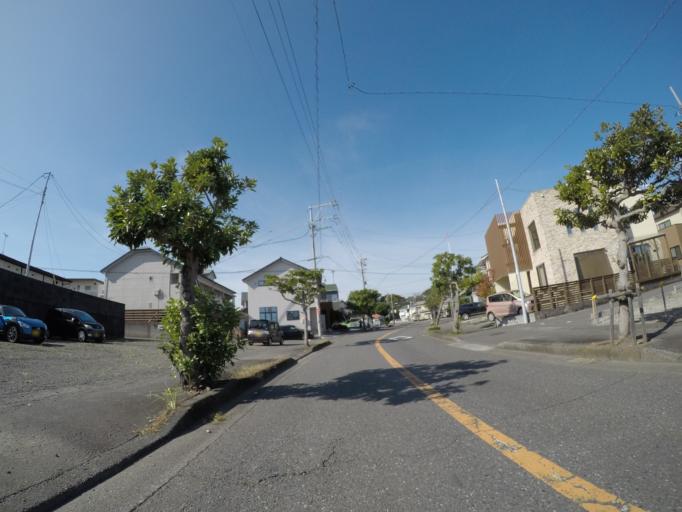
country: JP
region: Shizuoka
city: Shizuoka-shi
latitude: 34.9486
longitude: 138.4231
